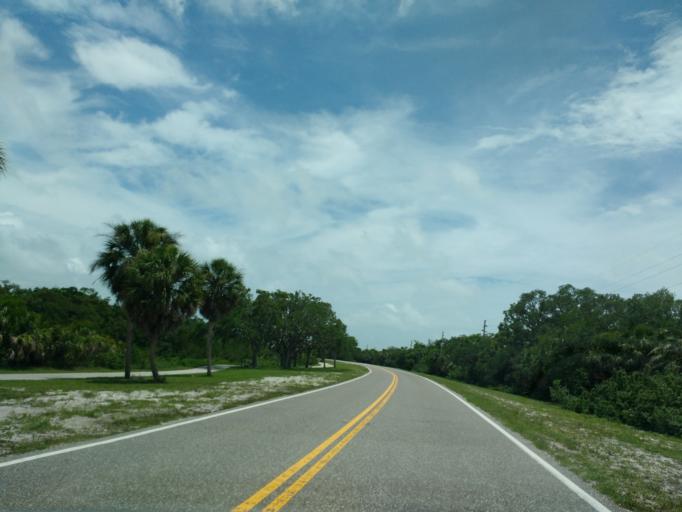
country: US
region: Florida
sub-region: Pinellas County
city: Tierra Verde
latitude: 27.6335
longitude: -82.7181
